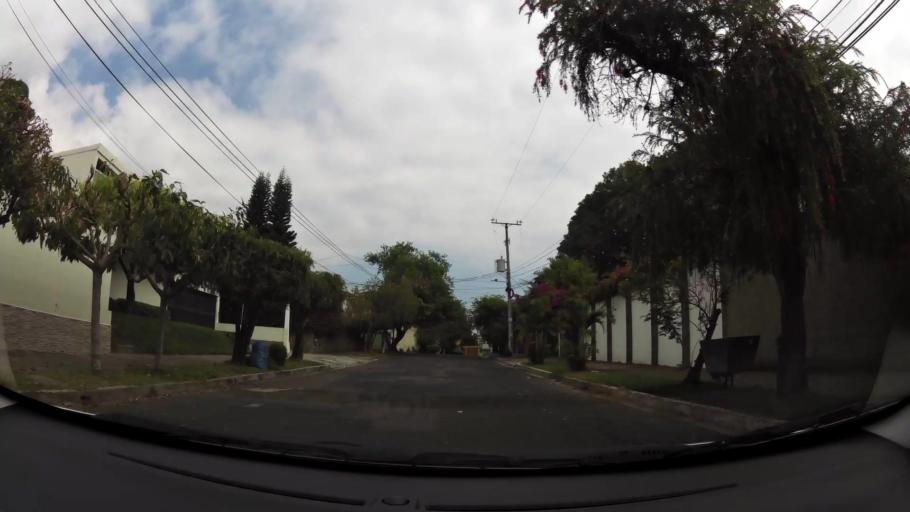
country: SV
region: La Libertad
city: Santa Tecla
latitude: 13.7066
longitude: -89.2581
